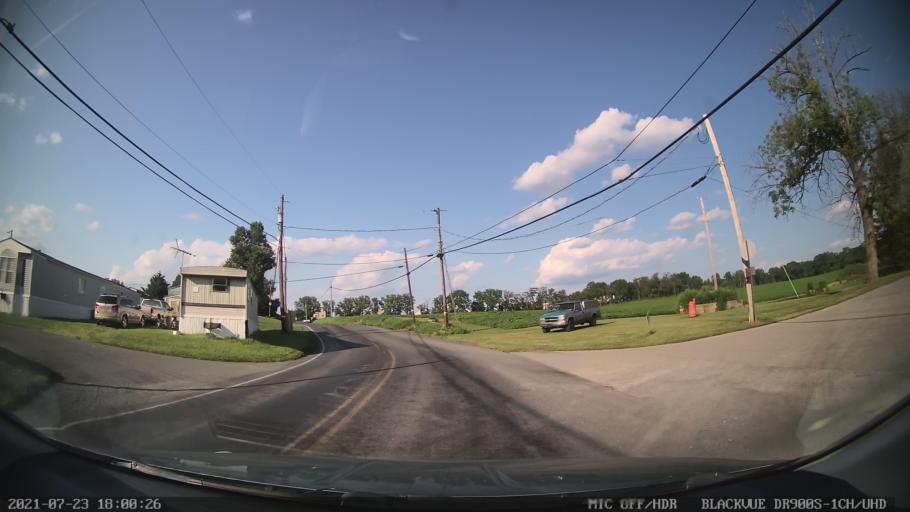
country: US
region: Pennsylvania
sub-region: Lehigh County
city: Macungie
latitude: 40.5245
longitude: -75.5258
